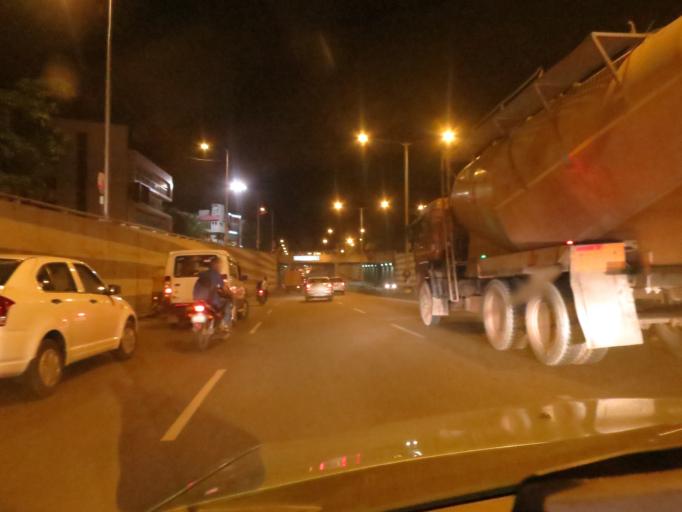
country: IN
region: Karnataka
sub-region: Bangalore Urban
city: Bangalore
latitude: 13.0120
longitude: 77.6623
